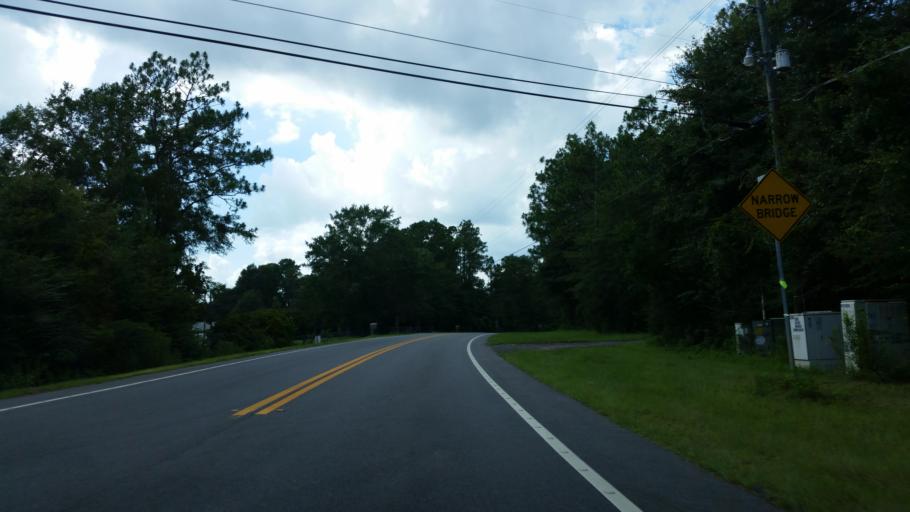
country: US
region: Florida
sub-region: Escambia County
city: Cantonment
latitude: 30.6343
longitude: -87.3813
